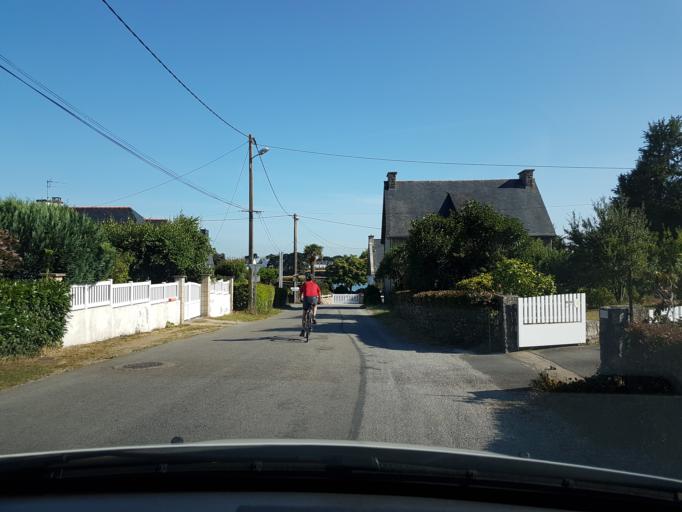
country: FR
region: Brittany
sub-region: Departement du Morbihan
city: Belz
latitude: 47.6762
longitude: -3.1890
